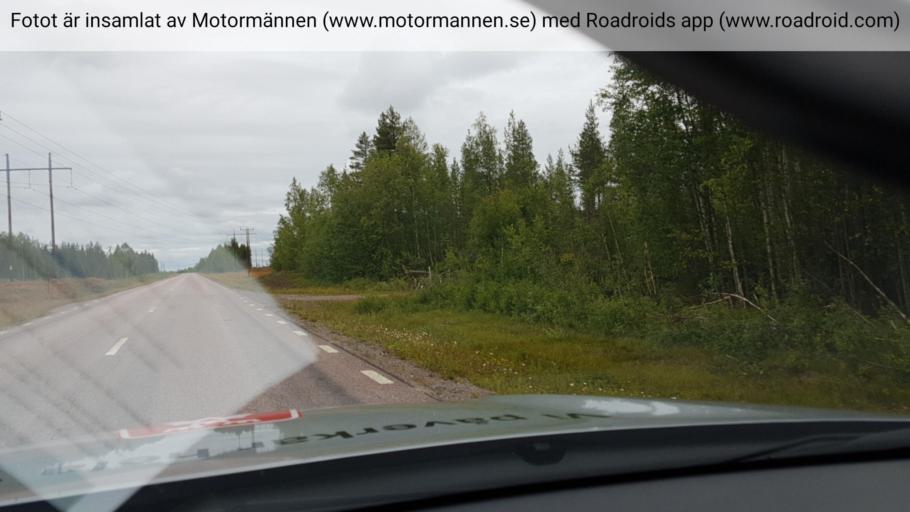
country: SE
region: Norrbotten
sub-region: Pajala Kommun
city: Pajala
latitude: 67.0929
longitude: 22.5694
